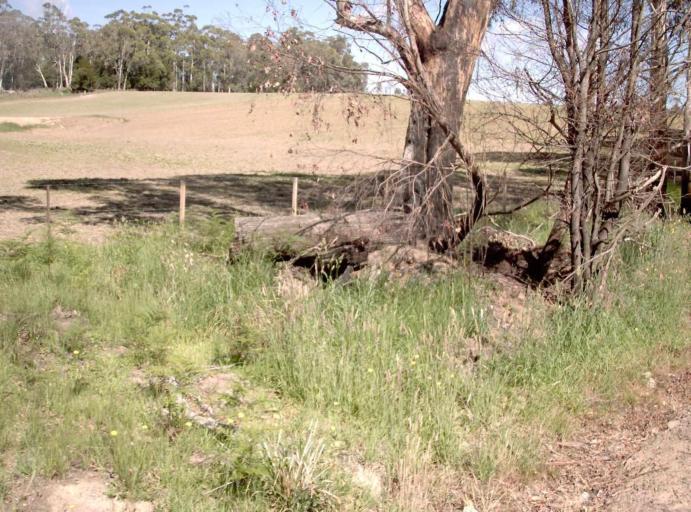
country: AU
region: New South Wales
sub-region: Bombala
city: Bombala
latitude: -37.1847
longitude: 148.7259
